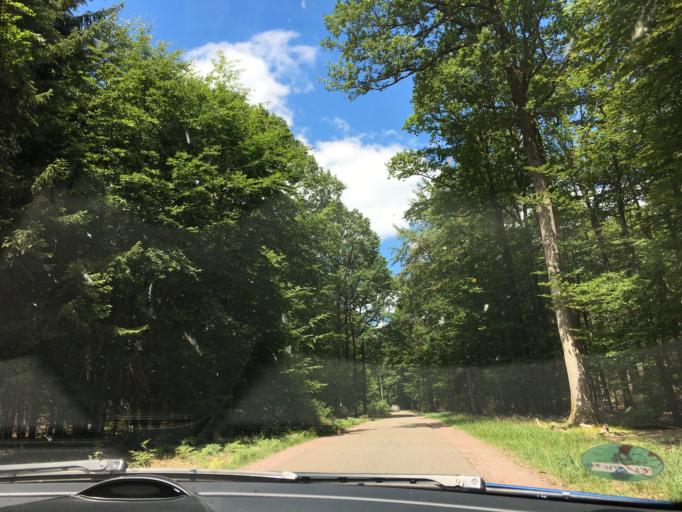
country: DE
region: Rheinland-Pfalz
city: Leimen
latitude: 49.2772
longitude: 7.8236
